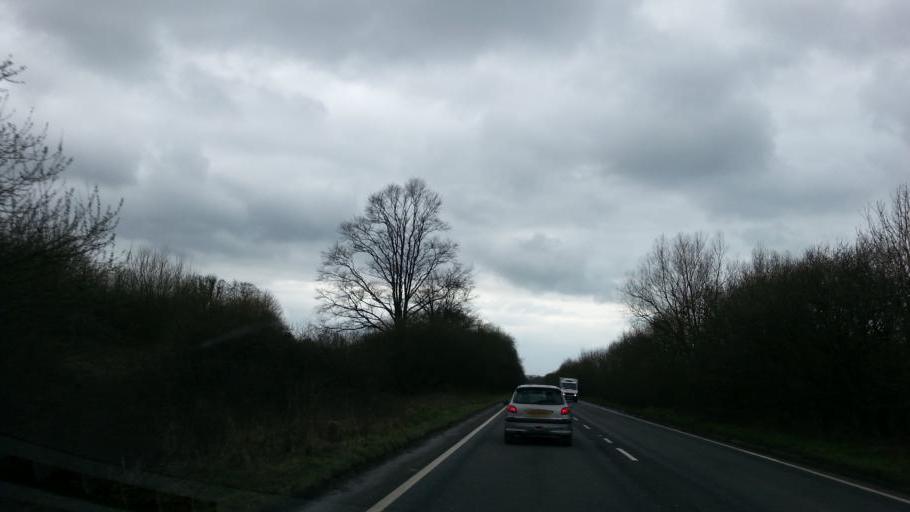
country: GB
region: England
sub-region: Devon
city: Barnstaple
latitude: 51.0691
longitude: -4.0161
